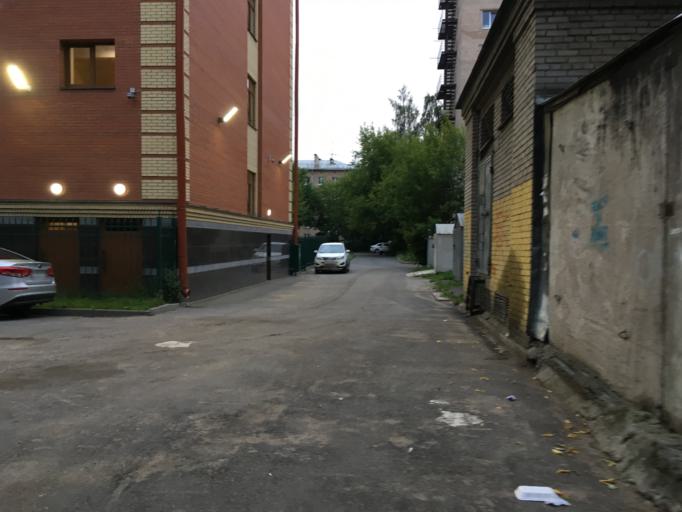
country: RU
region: St.-Petersburg
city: Vasyl'evsky Ostrov
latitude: 59.9354
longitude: 30.2454
